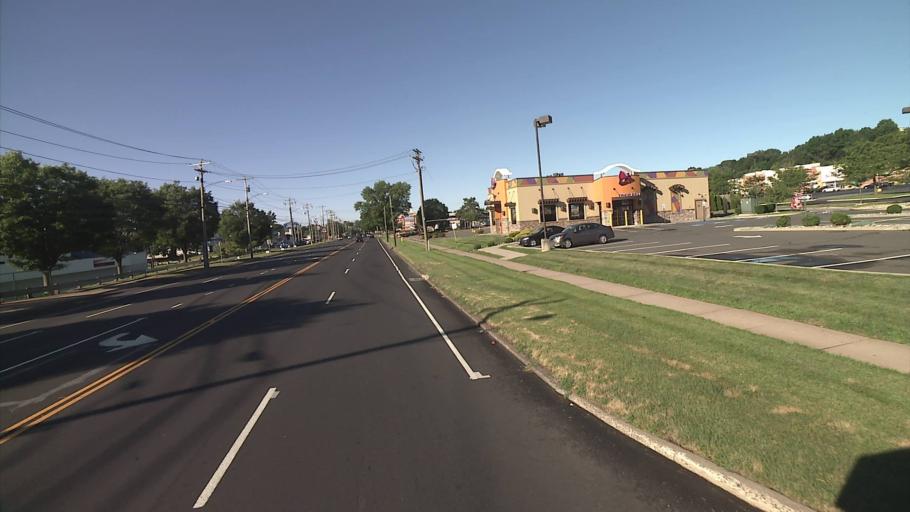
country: US
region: Connecticut
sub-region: New Haven County
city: Hamden
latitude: 41.3725
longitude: -72.9173
